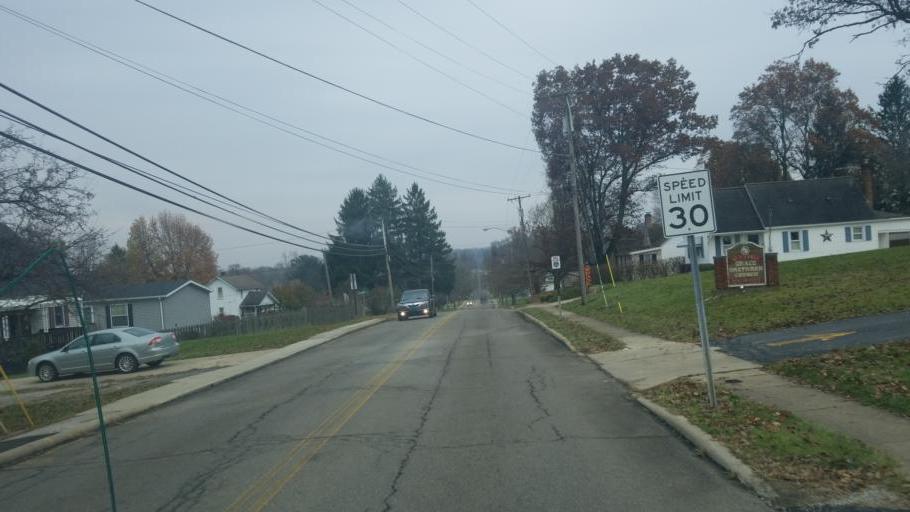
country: US
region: Ohio
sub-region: Richland County
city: Mansfield
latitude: 40.7421
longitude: -82.5037
